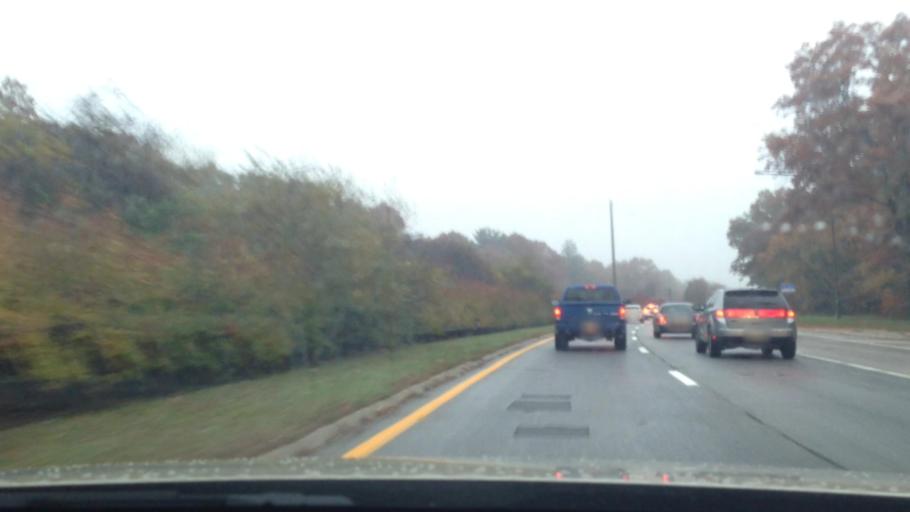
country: US
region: New York
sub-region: Suffolk County
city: Bay Wood
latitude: 40.7487
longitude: -73.2796
